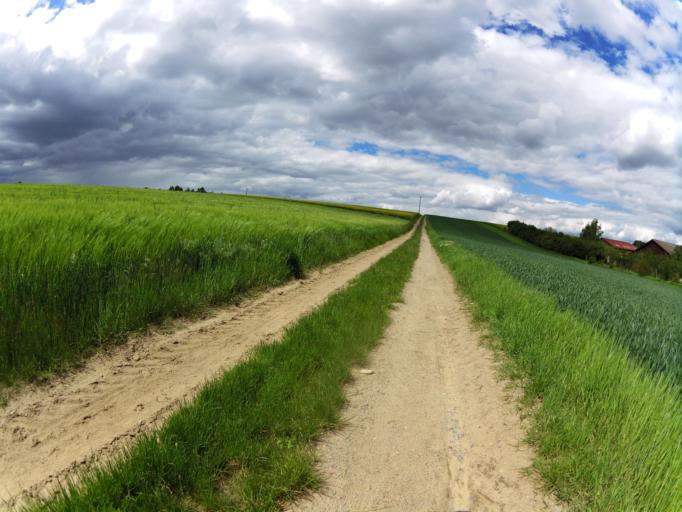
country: DE
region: Bavaria
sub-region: Regierungsbezirk Unterfranken
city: Volkach
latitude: 49.8700
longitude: 10.2463
